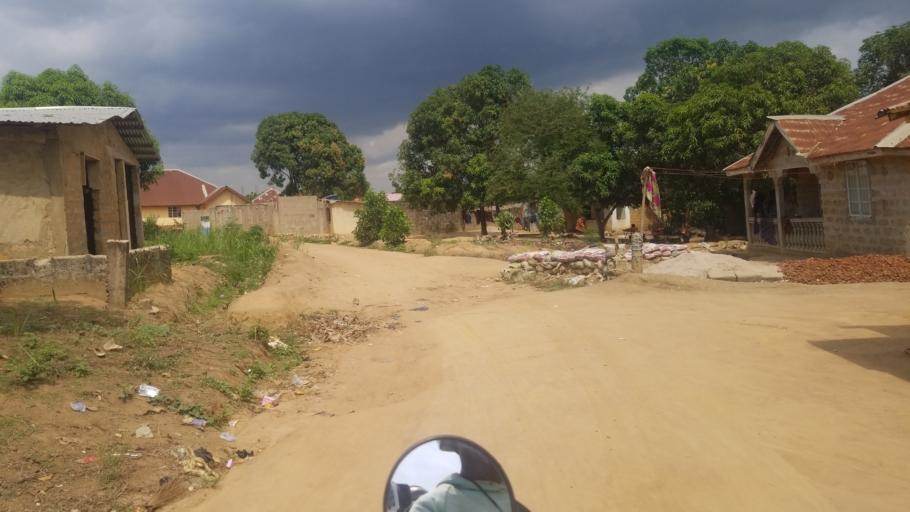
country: SL
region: Western Area
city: Waterloo
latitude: 8.3149
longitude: -13.0470
